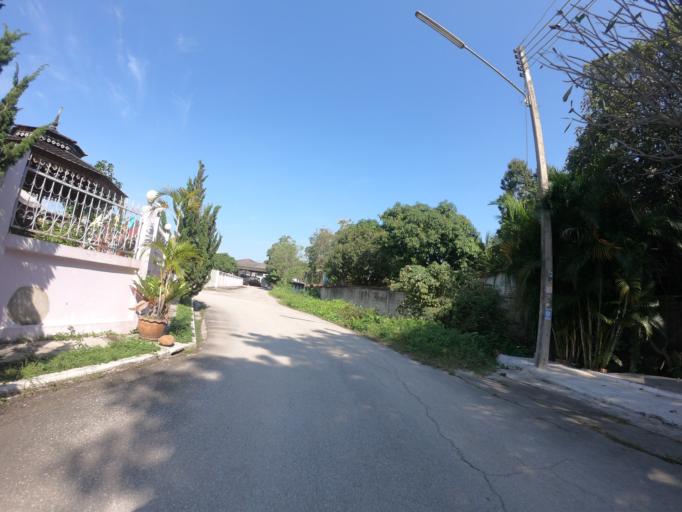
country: TH
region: Chiang Mai
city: Chiang Mai
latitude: 18.8059
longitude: 99.0073
